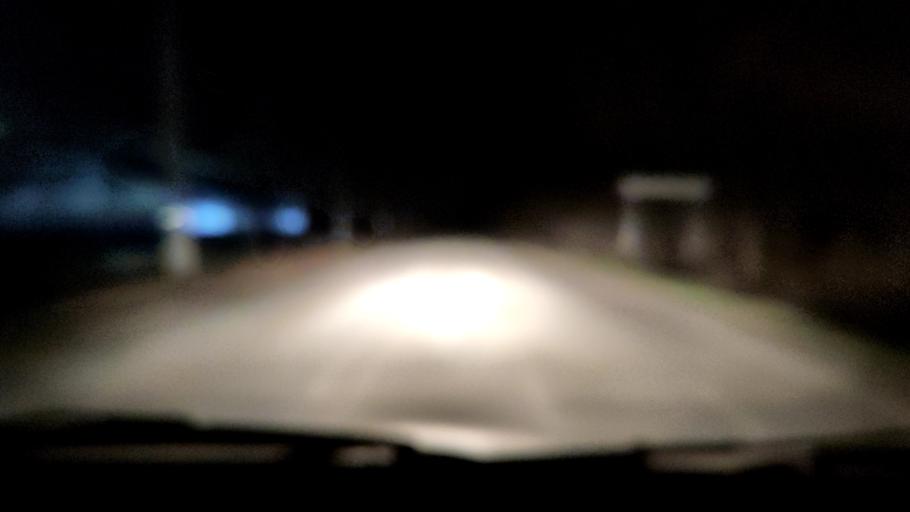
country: RU
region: Voronezj
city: Podkletnoye
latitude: 51.6434
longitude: 39.4850
